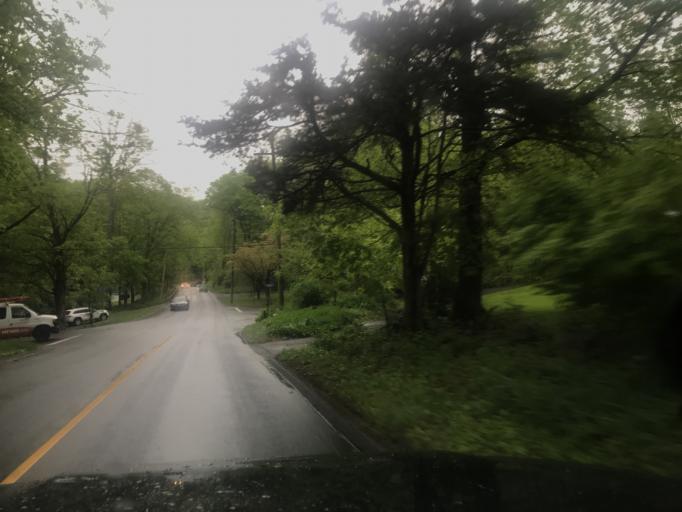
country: US
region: Connecticut
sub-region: Fairfield County
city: Bethel
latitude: 41.3900
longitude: -73.3940
